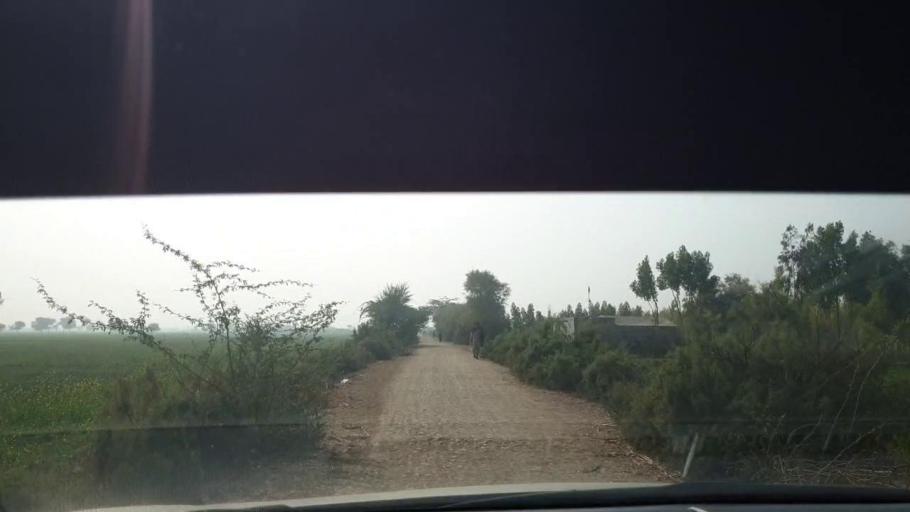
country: PK
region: Sindh
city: Berani
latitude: 25.7747
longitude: 68.8007
